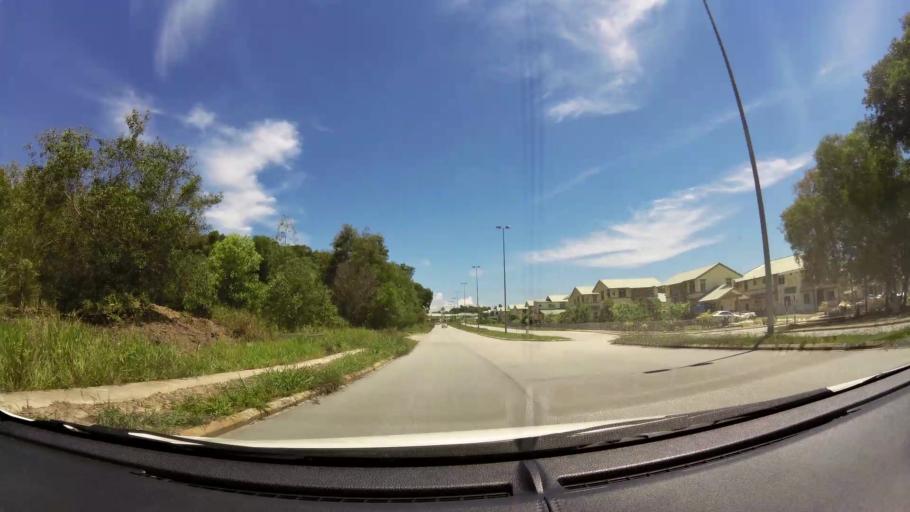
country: BN
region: Brunei and Muara
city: Bandar Seri Begawan
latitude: 5.0335
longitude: 115.0348
